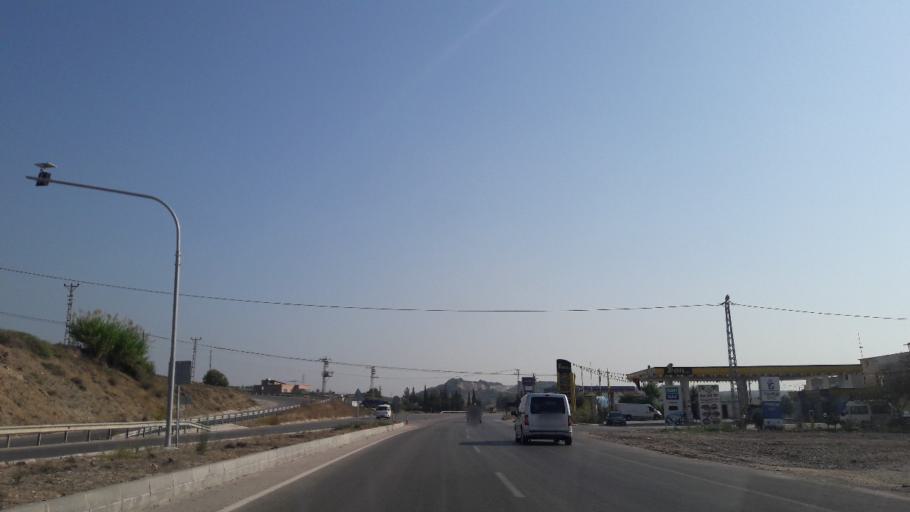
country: TR
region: Adana
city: Yuregir
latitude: 37.0709
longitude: 35.4579
